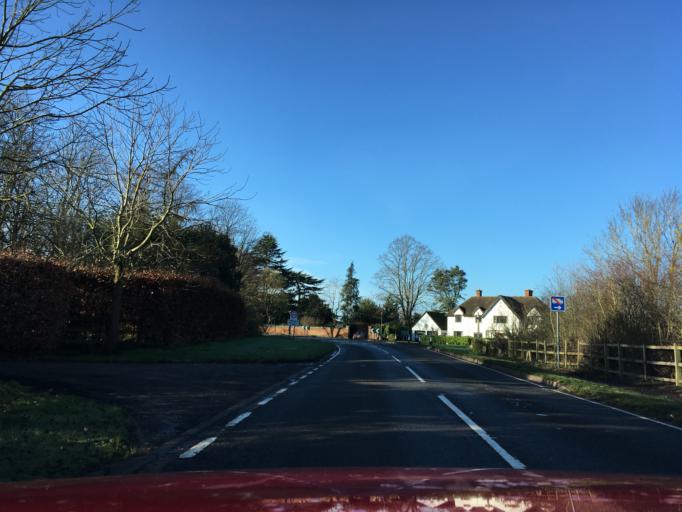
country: GB
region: England
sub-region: Warwickshire
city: Stratford-upon-Avon
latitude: 52.2033
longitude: -1.6662
